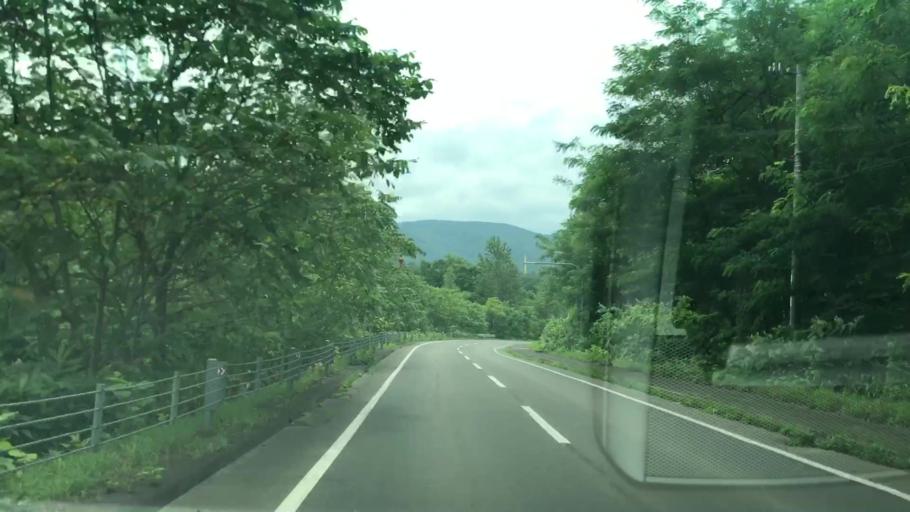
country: JP
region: Hokkaido
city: Yoichi
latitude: 43.0660
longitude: 140.8205
